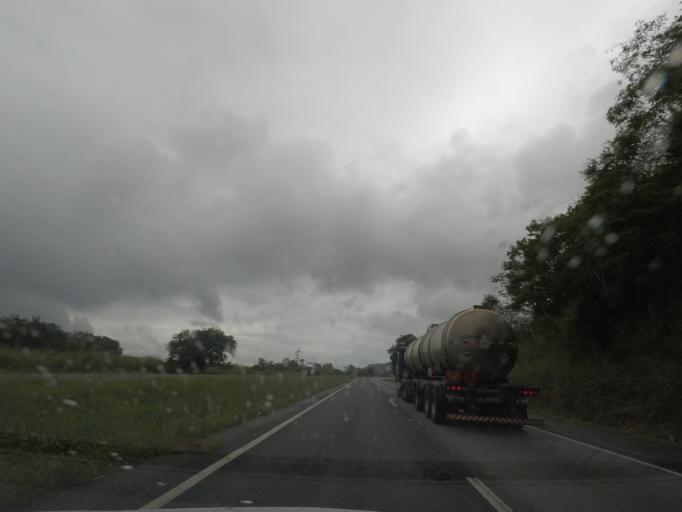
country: BR
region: Sao Paulo
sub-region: Miracatu
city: Miracatu
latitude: -24.3081
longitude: -47.5012
